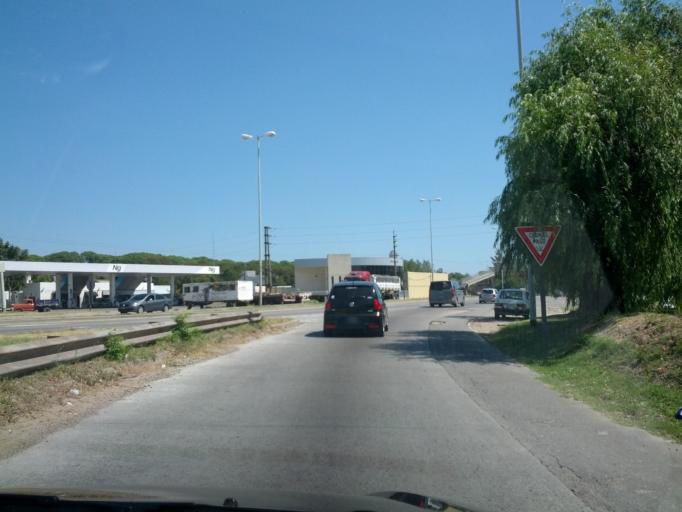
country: AR
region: Buenos Aires
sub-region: Partido de Campana
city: Campana
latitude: -34.1757
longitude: -58.9711
